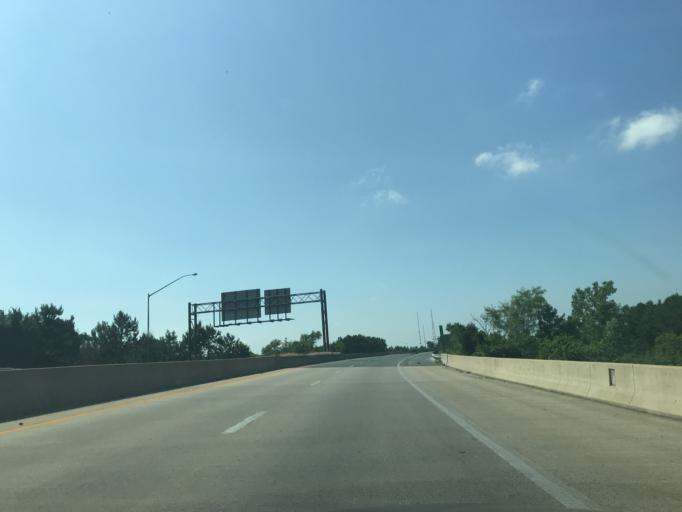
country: US
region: Maryland
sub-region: Wicomico County
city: Salisbury
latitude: 38.3976
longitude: -75.5711
